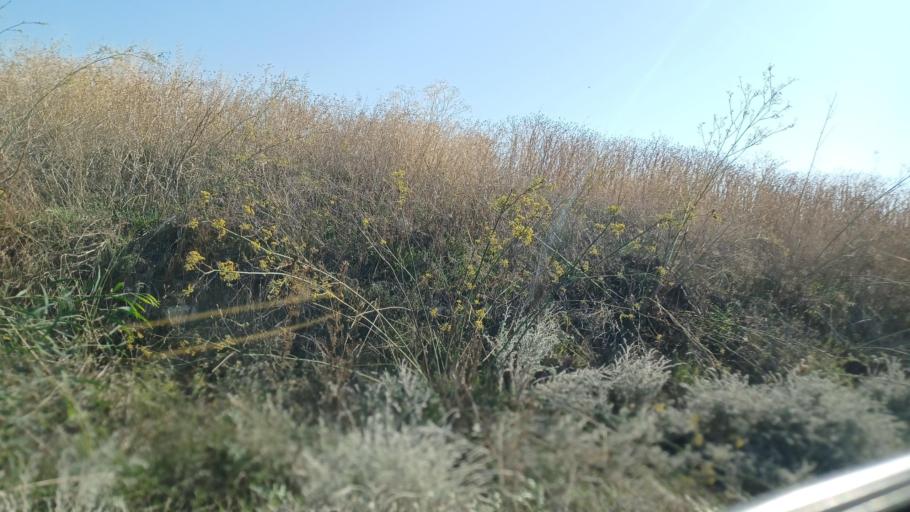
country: CY
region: Pafos
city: Polis
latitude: 35.0474
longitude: 32.4630
